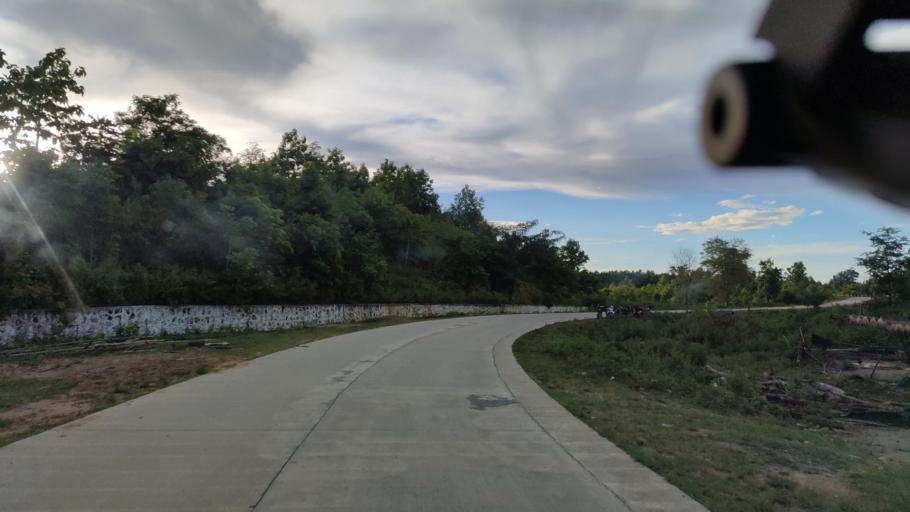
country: MM
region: Magway
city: Taungdwingyi
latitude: 20.0264
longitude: 95.7890
